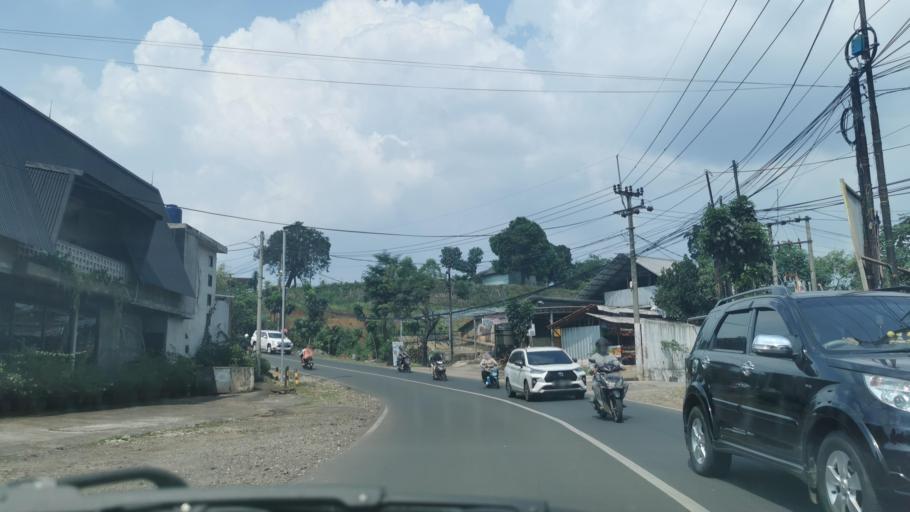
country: ID
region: West Java
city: Depok
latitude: -6.4081
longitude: 106.8335
